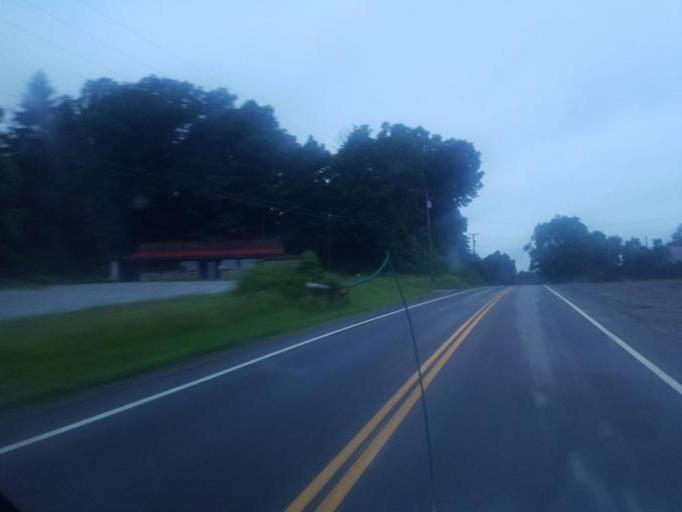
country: US
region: Ohio
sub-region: Carroll County
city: Carrollton
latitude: 40.5243
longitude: -81.0272
